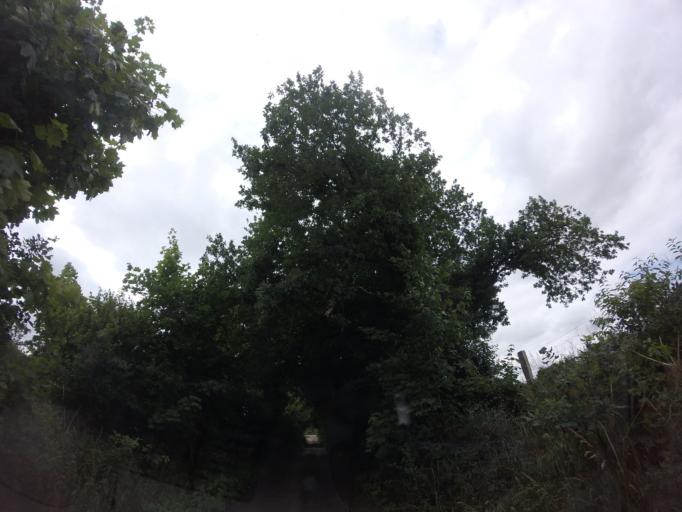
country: PL
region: West Pomeranian Voivodeship
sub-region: Powiat choszczenski
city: Bierzwnik
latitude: 52.9501
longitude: 15.6104
